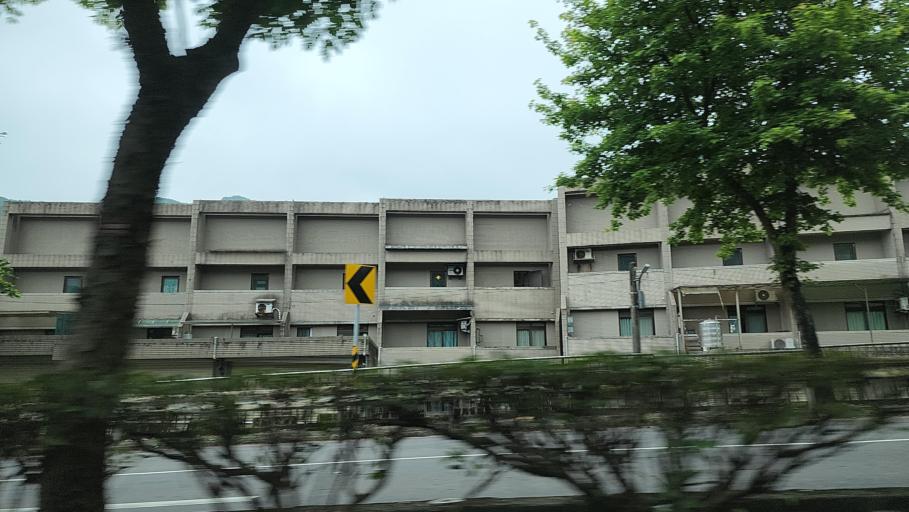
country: TW
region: Taiwan
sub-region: Keelung
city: Keelung
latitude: 25.1580
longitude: 121.6944
